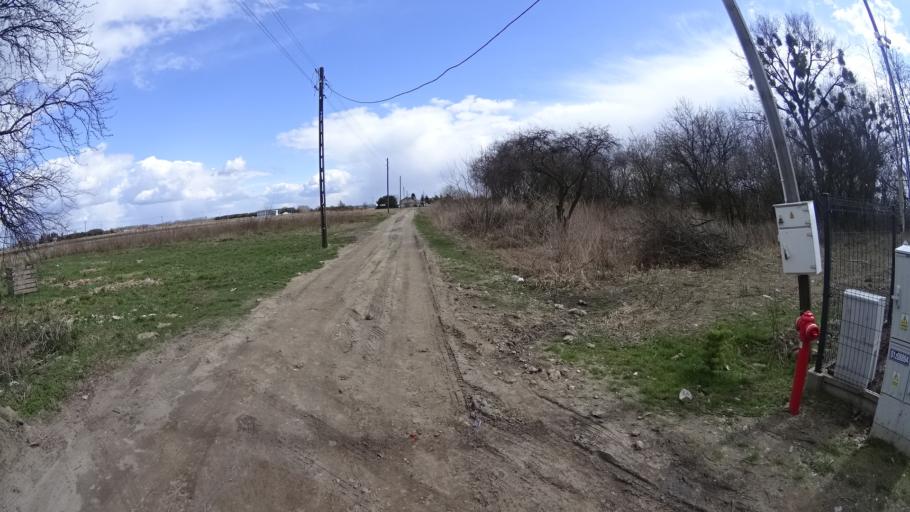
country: PL
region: Masovian Voivodeship
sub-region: Powiat warszawski zachodni
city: Jozefow
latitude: 52.2178
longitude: 20.7303
